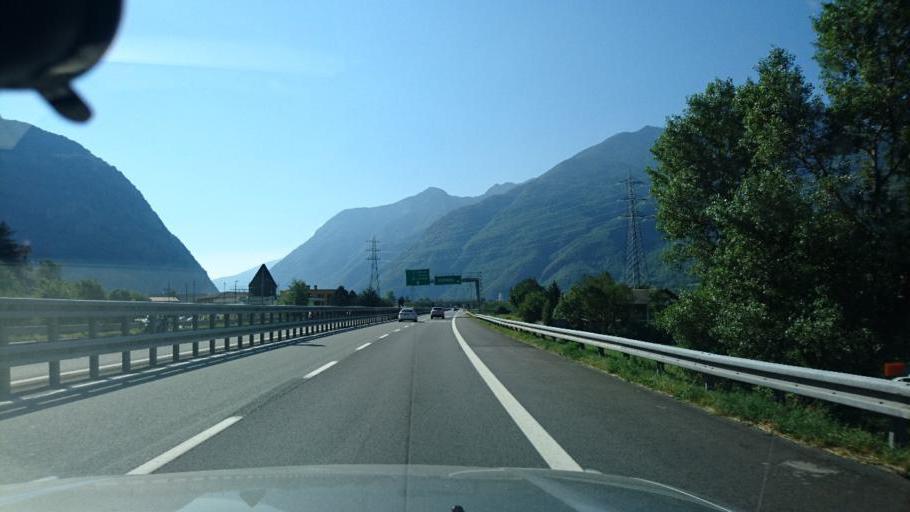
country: IT
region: Aosta Valley
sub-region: Valle d'Aosta
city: Verres
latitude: 45.6734
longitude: 7.6815
